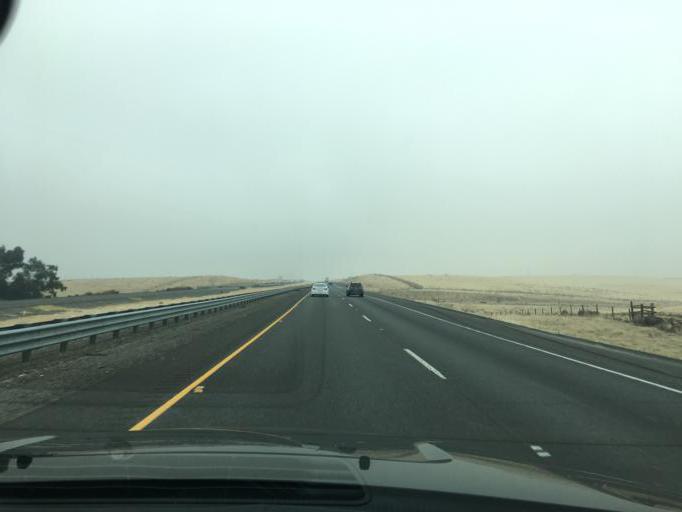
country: US
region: California
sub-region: Merced County
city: Los Banos
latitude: 37.0486
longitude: -120.9621
